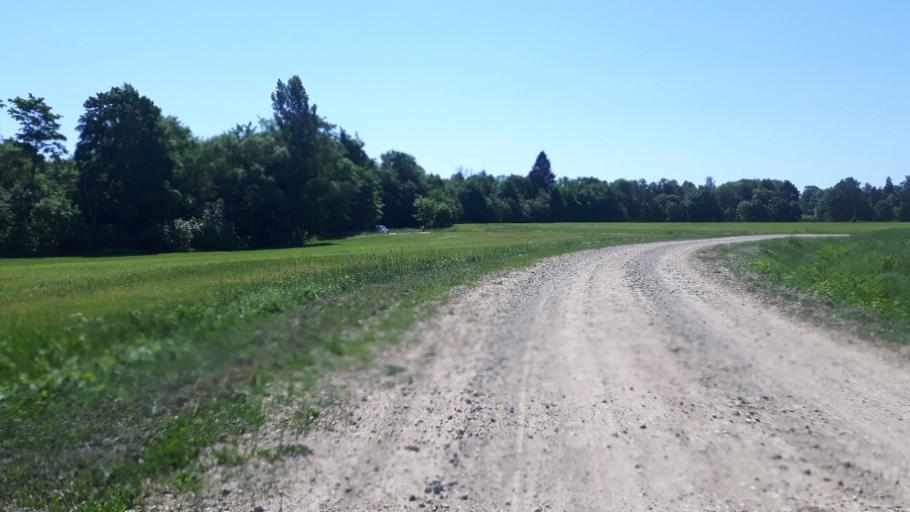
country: EE
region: Paernumaa
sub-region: Tootsi vald
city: Tootsi
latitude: 58.4968
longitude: 24.9004
